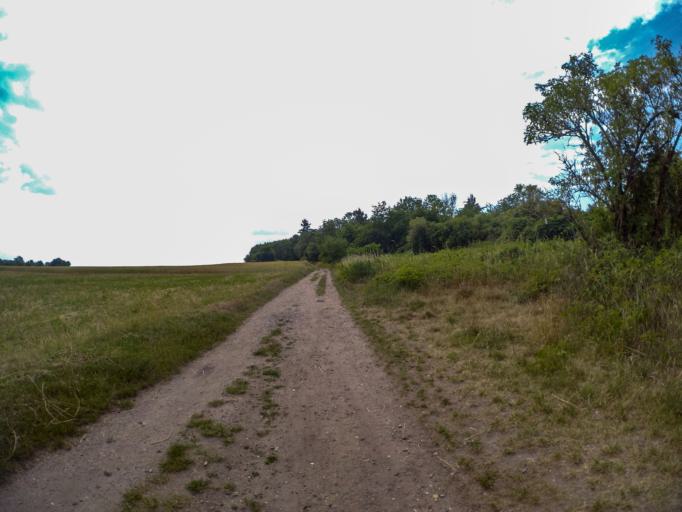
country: CZ
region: Central Bohemia
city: Neratovice
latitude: 50.2479
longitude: 14.5276
